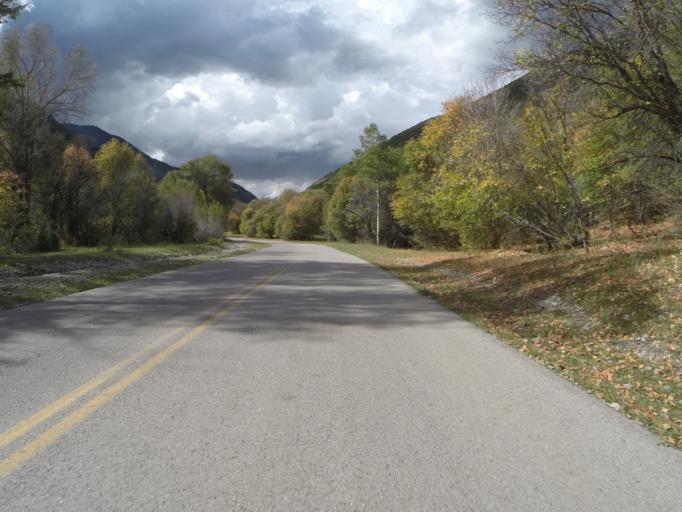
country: US
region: Utah
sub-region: Tooele County
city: Tooele
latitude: 40.4893
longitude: -112.1964
